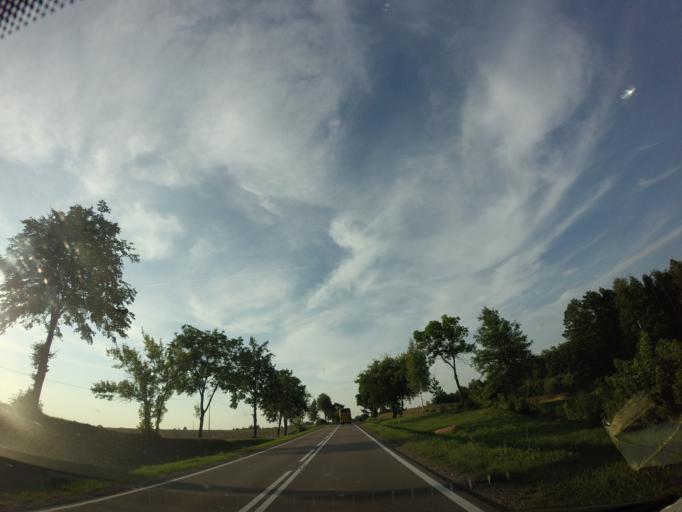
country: PL
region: Podlasie
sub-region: Powiat sejnenski
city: Sejny
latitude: 54.0500
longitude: 23.3550
